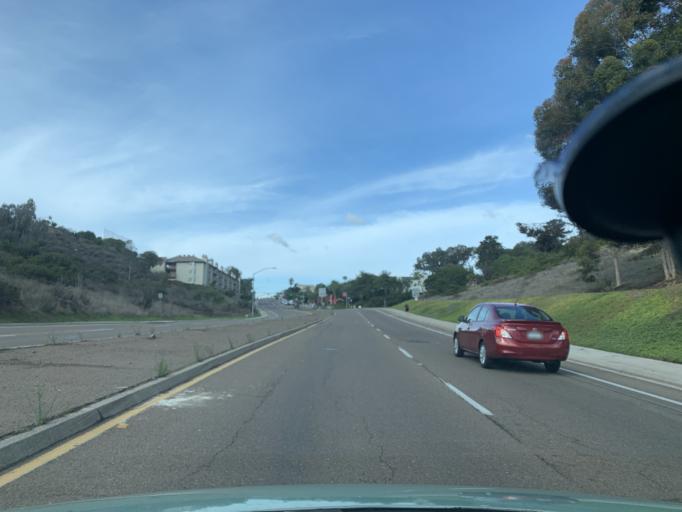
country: US
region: California
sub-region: San Diego County
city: San Diego
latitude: 32.8117
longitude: -117.1782
